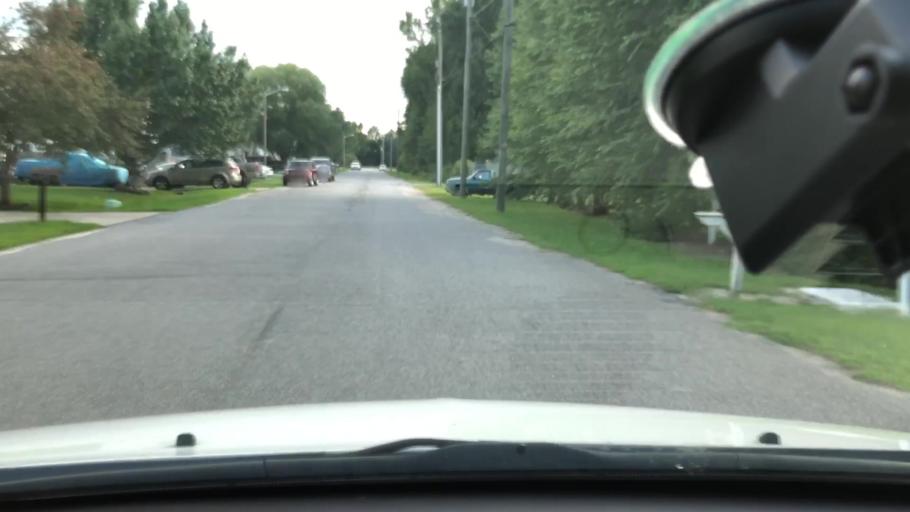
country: US
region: Virginia
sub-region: City of Chesapeake
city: Chesapeake
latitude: 36.7211
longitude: -76.2694
